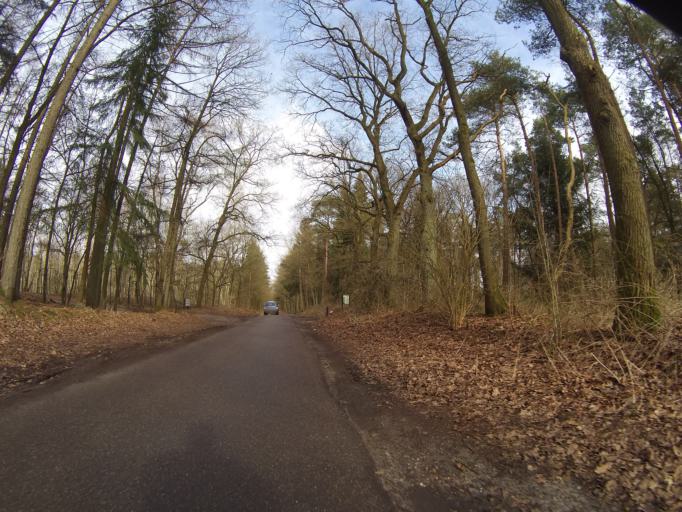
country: NL
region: Utrecht
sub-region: Gemeente Amersfoort
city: Hoogland
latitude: 52.1528
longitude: 5.3375
